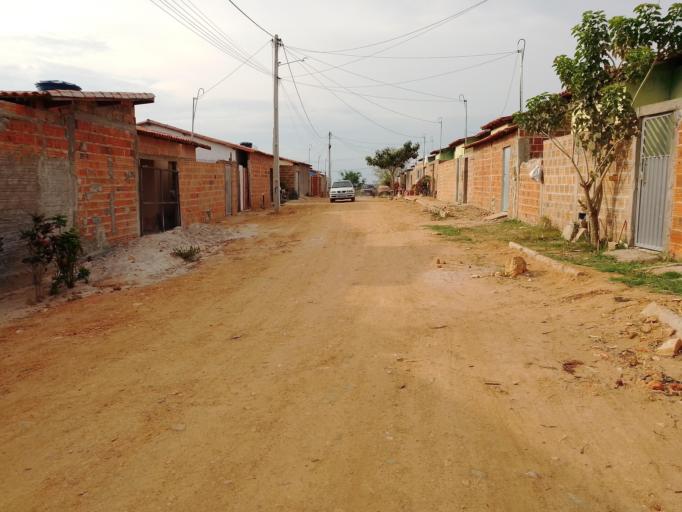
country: BR
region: Bahia
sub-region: Brumado
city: Brumado
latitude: -14.4420
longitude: -41.4627
